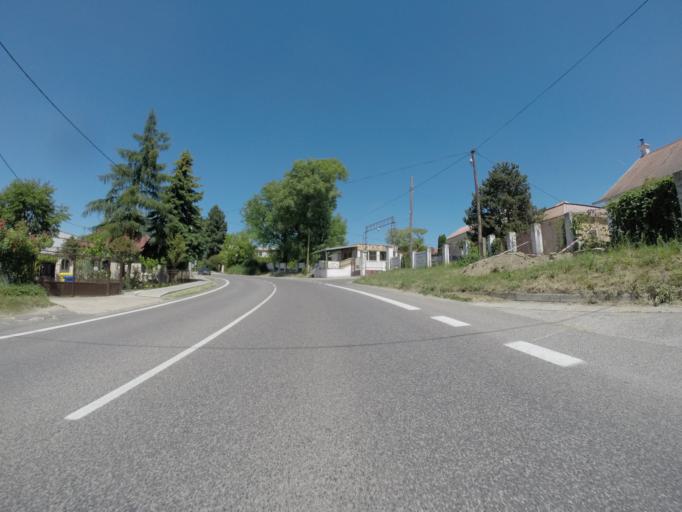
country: SK
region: Trnavsky
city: Hlohovec
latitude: 48.4440
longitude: 17.8114
